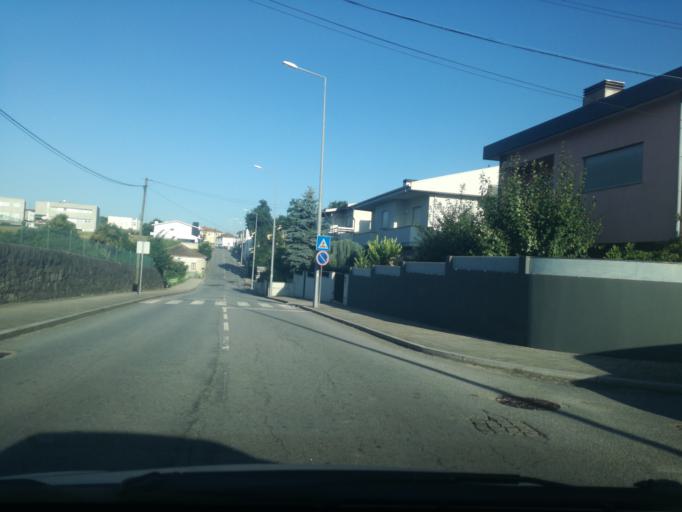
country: PT
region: Porto
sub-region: Valongo
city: Ermesinde
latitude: 41.2295
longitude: -8.5566
